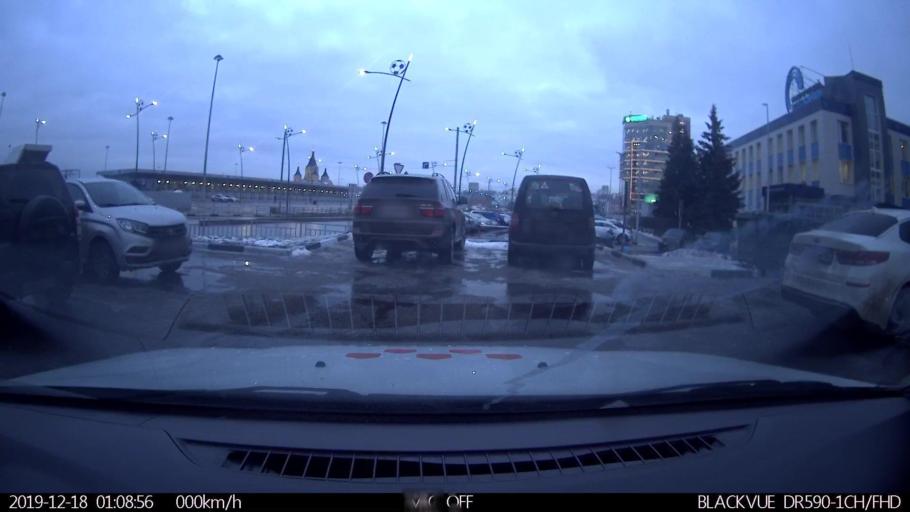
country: RU
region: Nizjnij Novgorod
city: Nizhniy Novgorod
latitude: 56.3343
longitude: 43.9604
